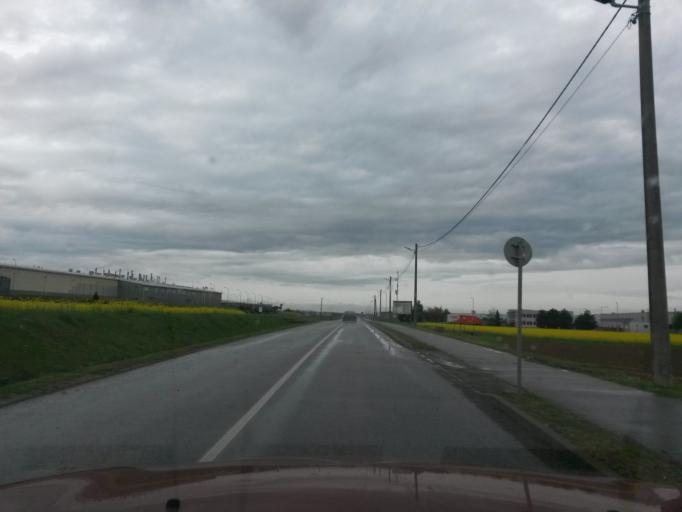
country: HU
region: Borsod-Abauj-Zemplen
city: Gonc
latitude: 48.5518
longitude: 21.2543
